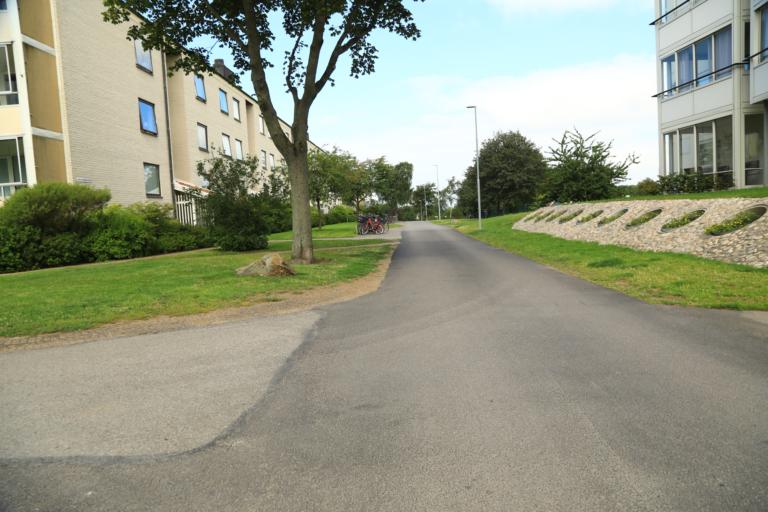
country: SE
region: Halland
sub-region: Varbergs Kommun
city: Varberg
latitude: 57.0949
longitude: 12.2633
